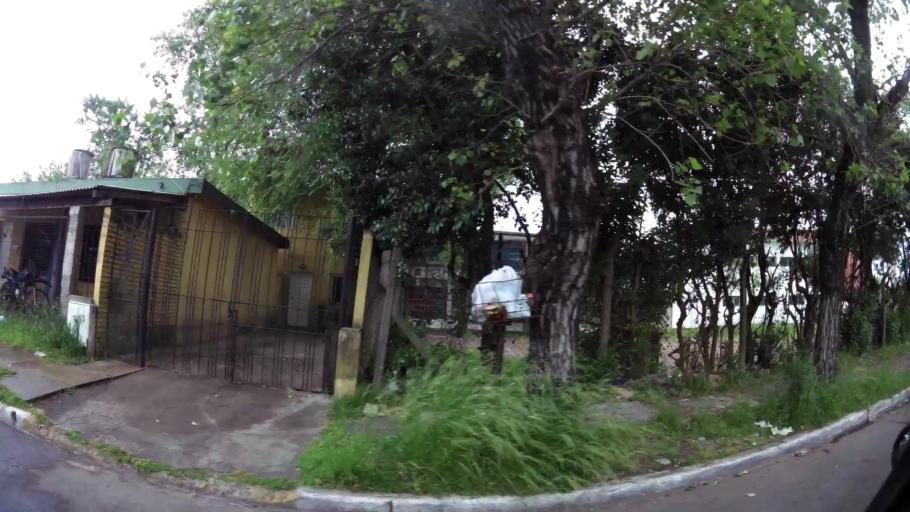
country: AR
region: Buenos Aires
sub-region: Partido de Quilmes
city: Quilmes
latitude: -34.7588
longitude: -58.2015
